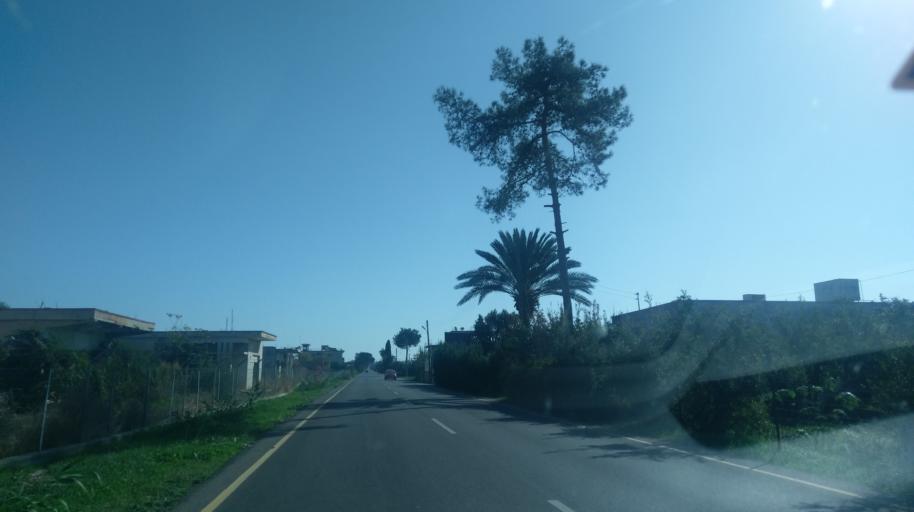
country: CY
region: Ammochostos
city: Famagusta
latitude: 35.0970
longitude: 33.9508
